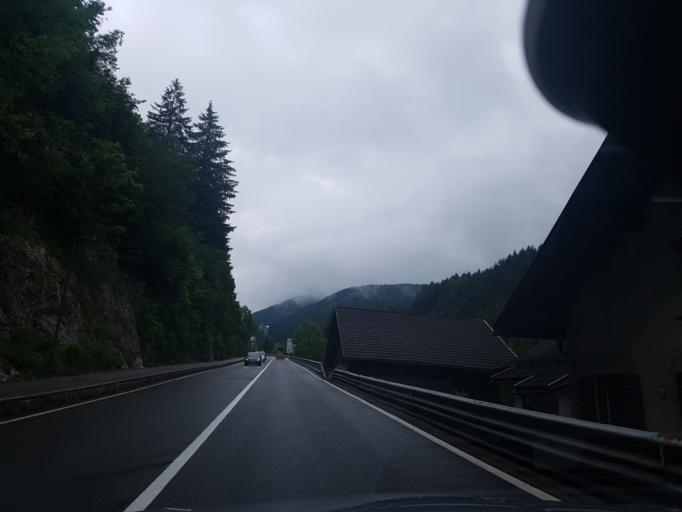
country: IT
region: Trentino-Alto Adige
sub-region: Bolzano
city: Santa Cristina Valgardena
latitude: 46.5584
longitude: 11.7141
